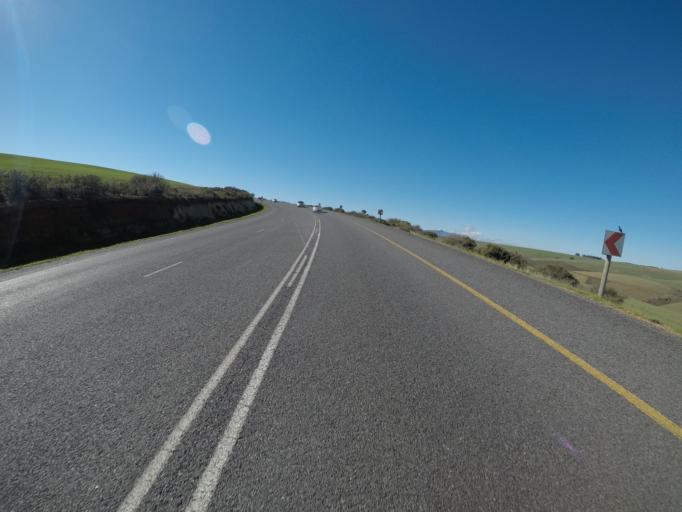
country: ZA
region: Western Cape
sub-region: Overberg District Municipality
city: Caledon
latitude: -34.2289
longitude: 19.2712
